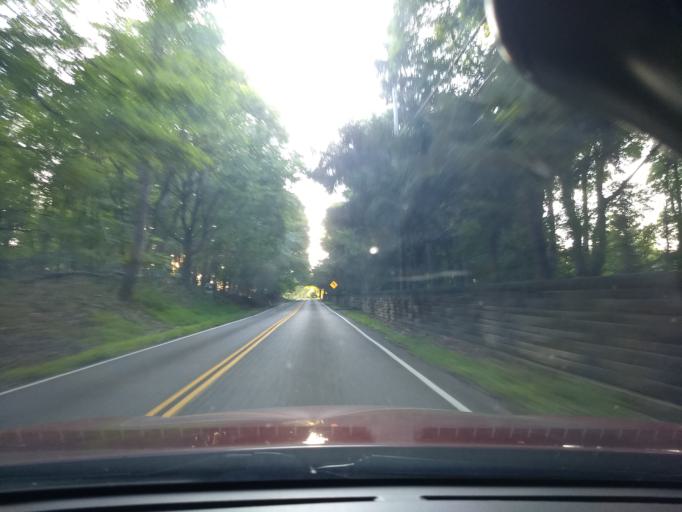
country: US
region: Pennsylvania
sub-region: Allegheny County
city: Sewickley
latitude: 40.5514
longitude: -80.1569
